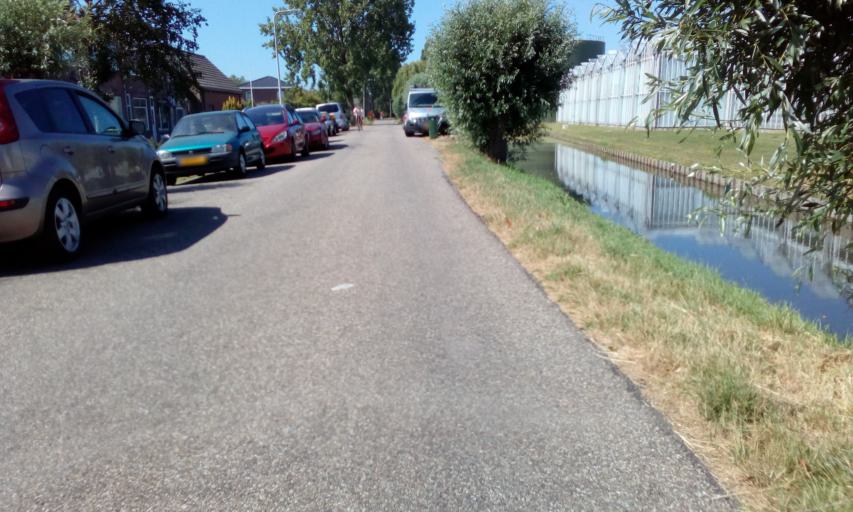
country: NL
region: South Holland
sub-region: Gemeente Westland
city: De Lier
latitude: 51.9805
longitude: 4.2793
